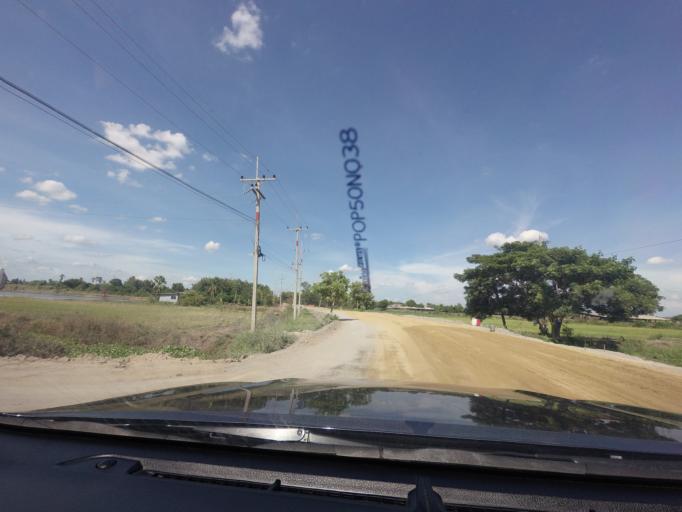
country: TH
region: Suphan Buri
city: Song Phi Nong
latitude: 14.1801
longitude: 100.0439
